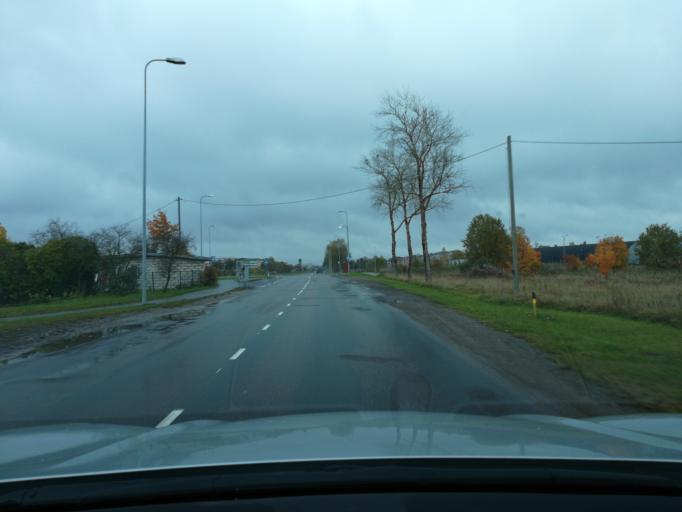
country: EE
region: Ida-Virumaa
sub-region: Johvi vald
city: Johvi
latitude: 59.3353
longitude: 27.4050
